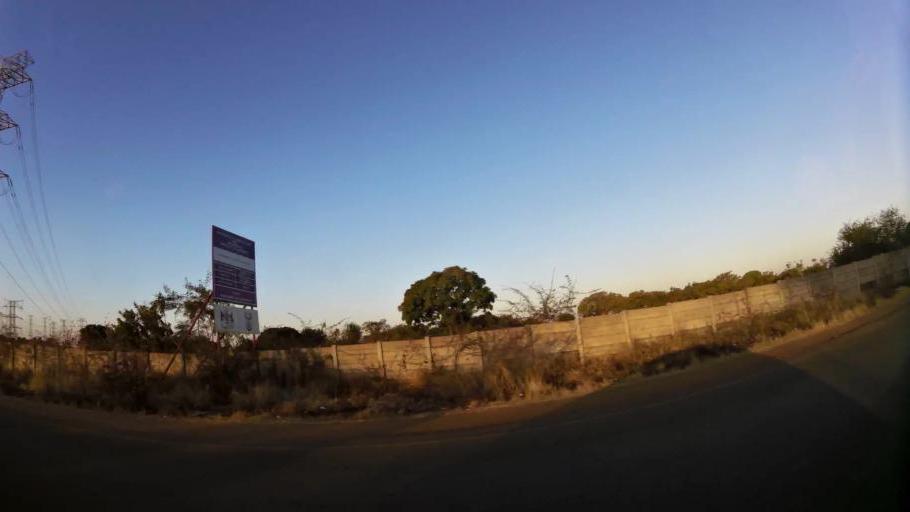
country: ZA
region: North-West
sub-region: Bojanala Platinum District Municipality
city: Rustenburg
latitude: -25.6322
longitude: 27.2024
